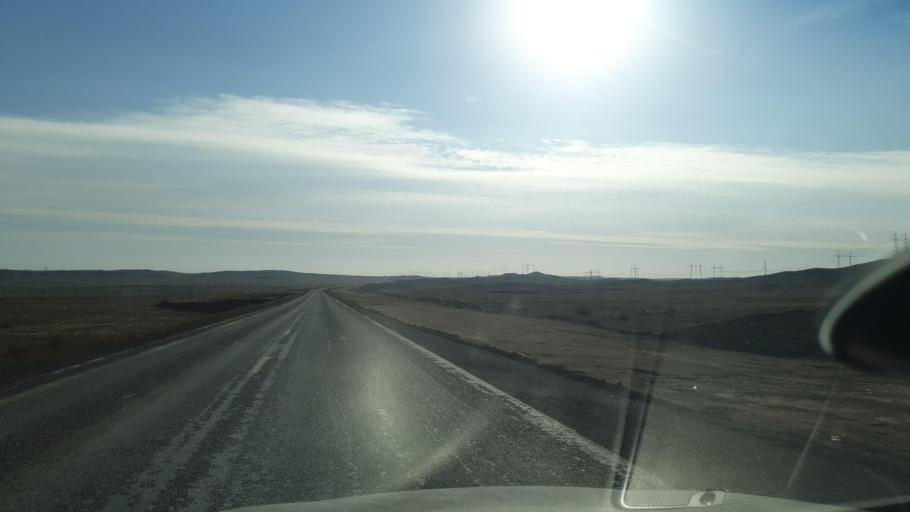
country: KZ
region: Zhambyl
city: Mynaral
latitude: 45.6899
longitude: 73.4004
